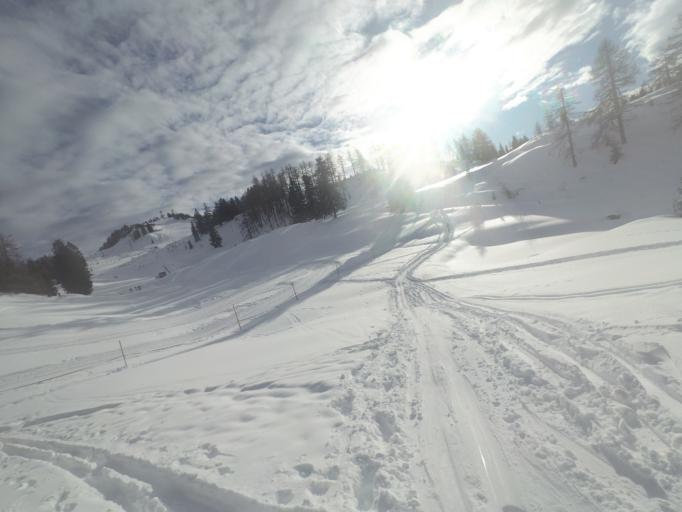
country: AT
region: Salzburg
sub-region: Politischer Bezirk Sankt Johann im Pongau
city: Sankt Johann im Pongau
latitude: 47.3104
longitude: 13.2217
